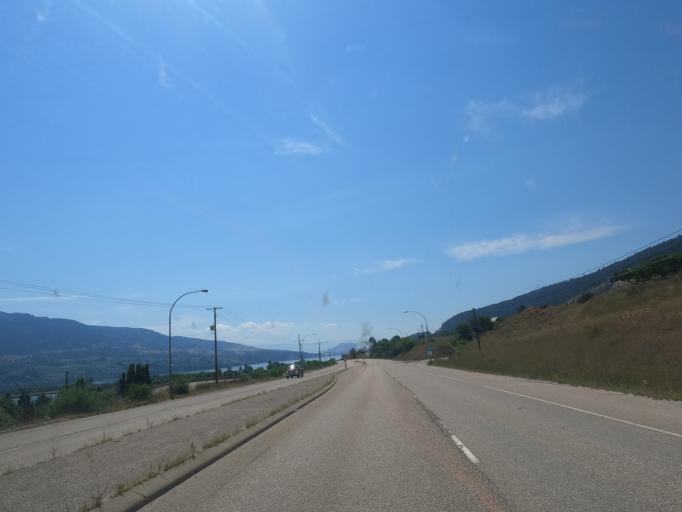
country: CA
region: British Columbia
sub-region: Regional District of North Okanagan
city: Vernon
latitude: 50.1197
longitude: -119.3871
